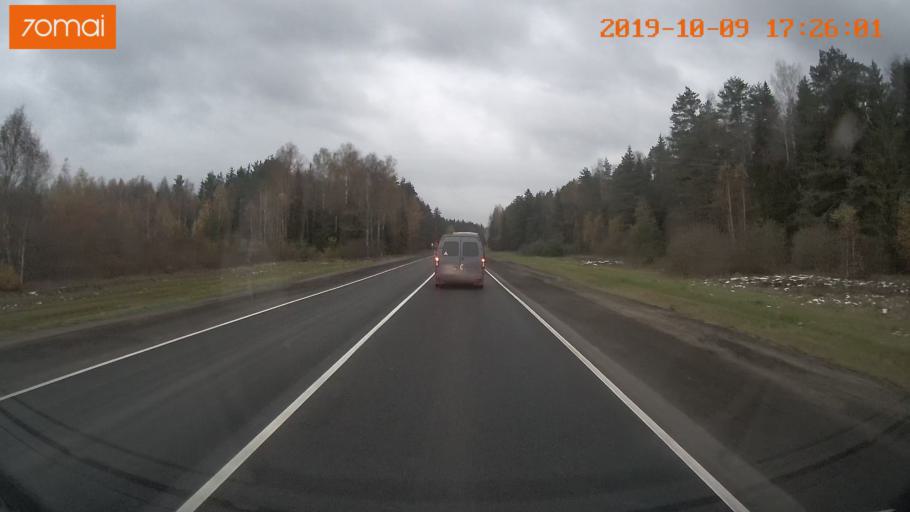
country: RU
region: Ivanovo
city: Furmanov
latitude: 57.1771
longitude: 41.0826
